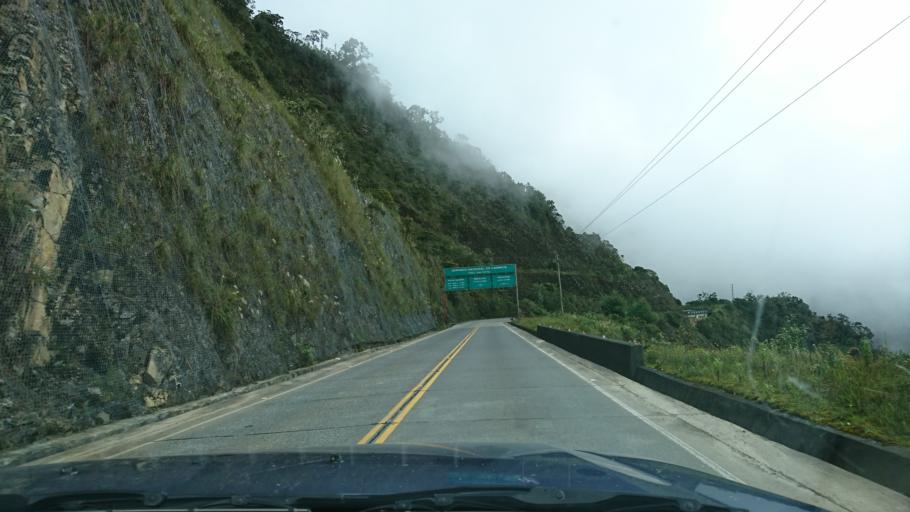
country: BO
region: La Paz
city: Coroico
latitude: -16.2706
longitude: -67.8242
